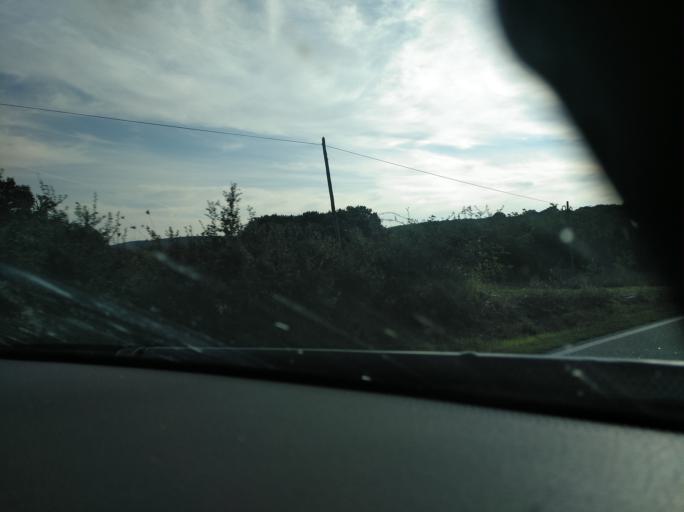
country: PT
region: Portalegre
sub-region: Fronteira
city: Fronteira
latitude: 38.9589
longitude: -7.6277
